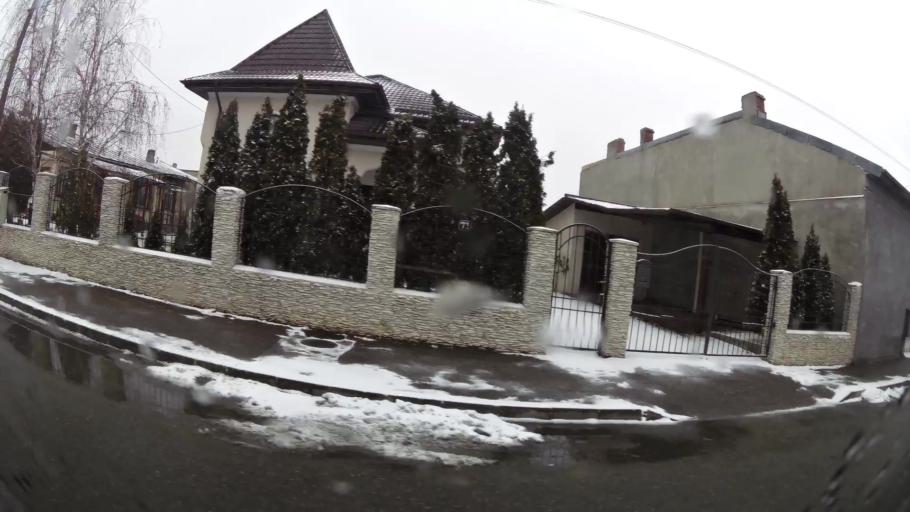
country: RO
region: Dambovita
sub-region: Municipiul Targoviste
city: Targoviste
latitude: 44.9379
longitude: 25.4475
